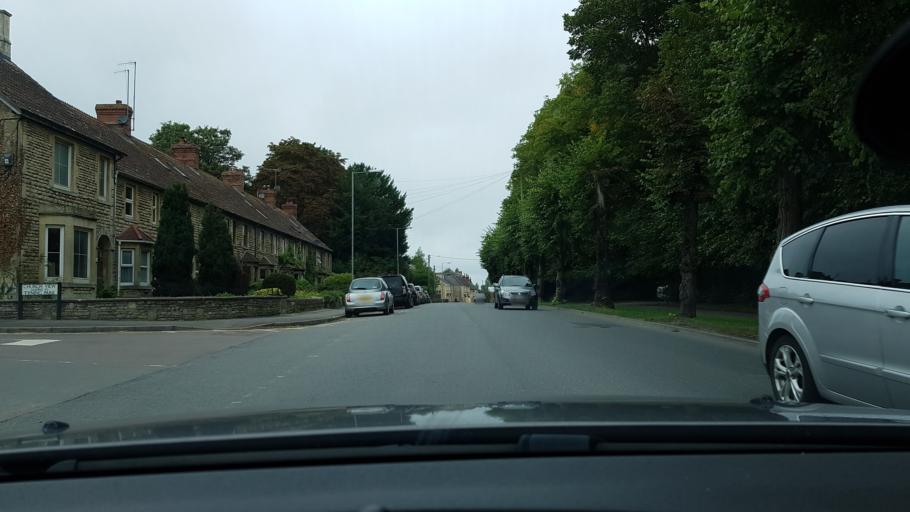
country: GB
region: England
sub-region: Wiltshire
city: Calne
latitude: 51.4299
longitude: -1.9974
